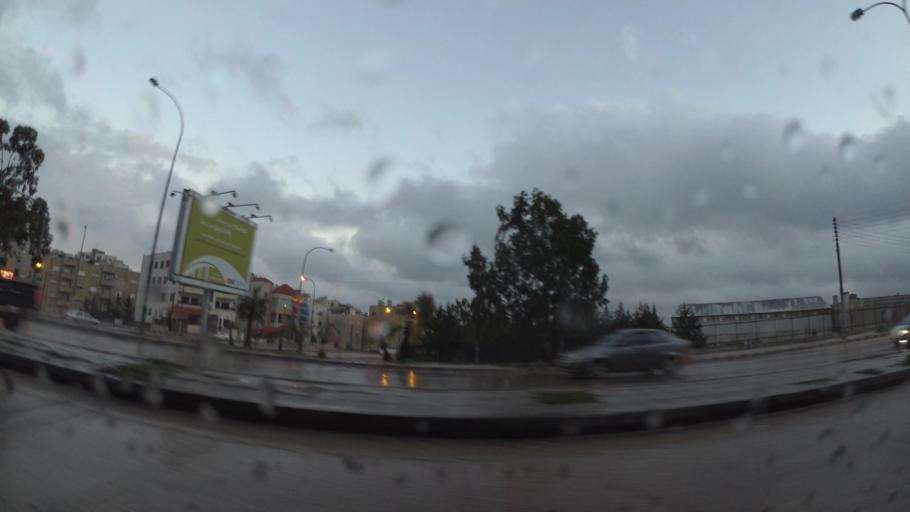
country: JO
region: Amman
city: Amman
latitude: 31.9894
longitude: 35.9094
